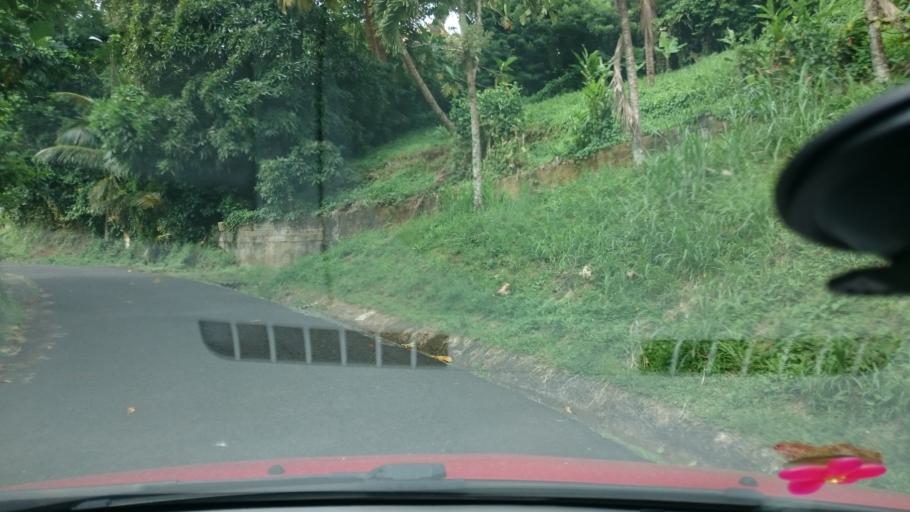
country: MQ
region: Martinique
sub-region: Martinique
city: Riviere-Pilote
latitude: 14.4974
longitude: -60.9208
